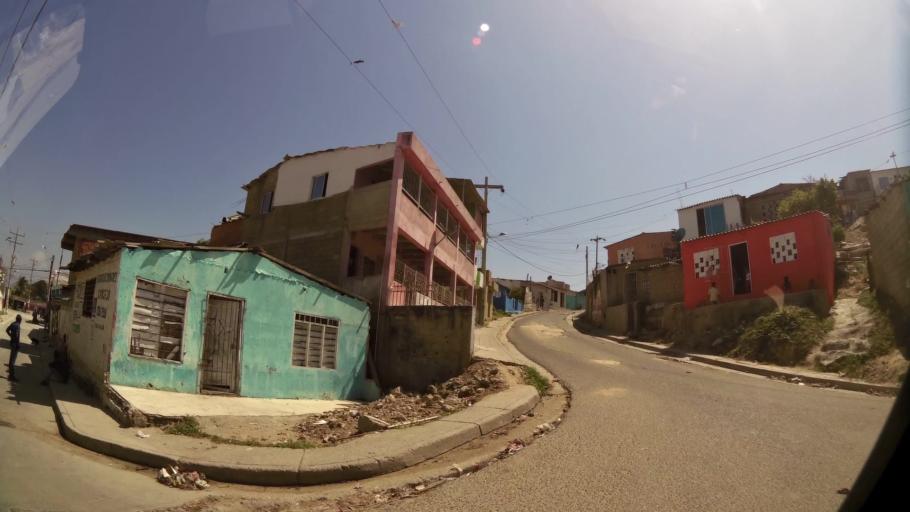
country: CO
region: Bolivar
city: Cartagena
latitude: 10.4347
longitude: -75.5250
